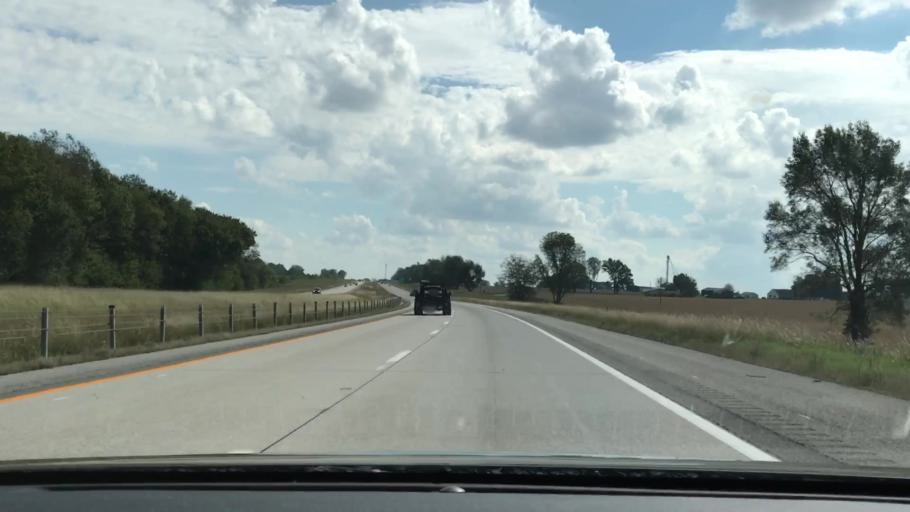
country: US
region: Kentucky
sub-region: Christian County
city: Hopkinsville
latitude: 36.8288
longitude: -87.6603
